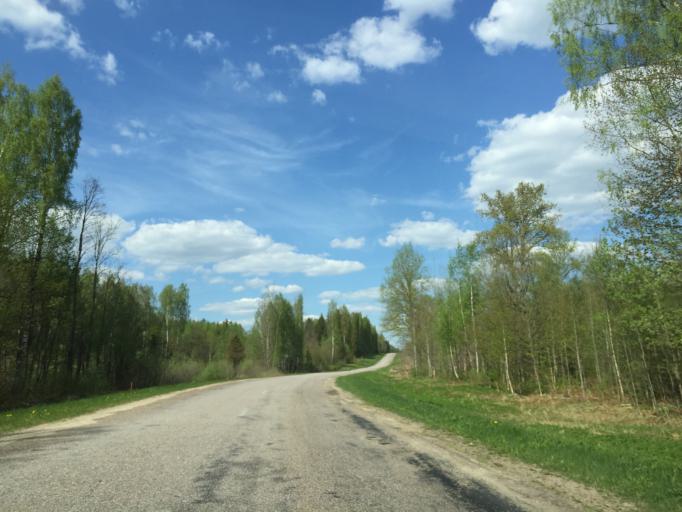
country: LV
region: Limbazu Rajons
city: Limbazi
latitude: 57.4060
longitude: 24.6910
